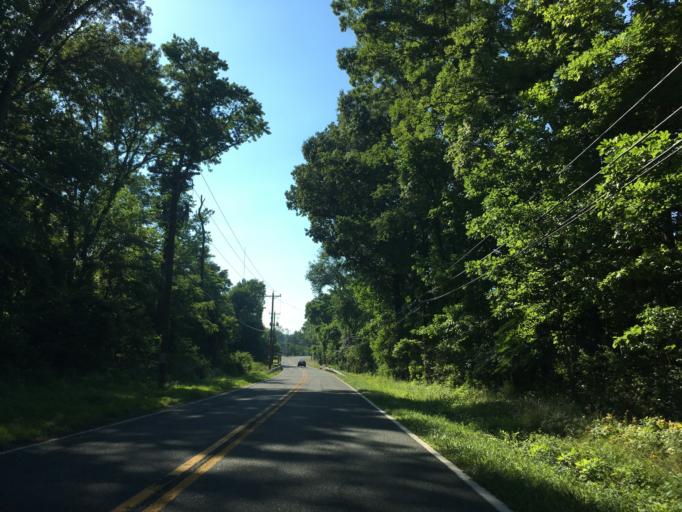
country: US
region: Maryland
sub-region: Queen Anne's County
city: Grasonville
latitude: 38.9838
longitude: -76.1453
